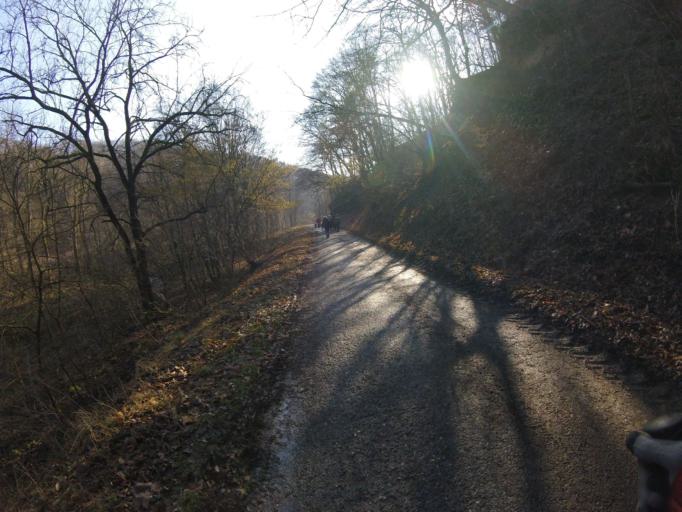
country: HU
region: Komarom-Esztergom
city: Pilismarot
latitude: 47.7510
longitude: 18.9032
